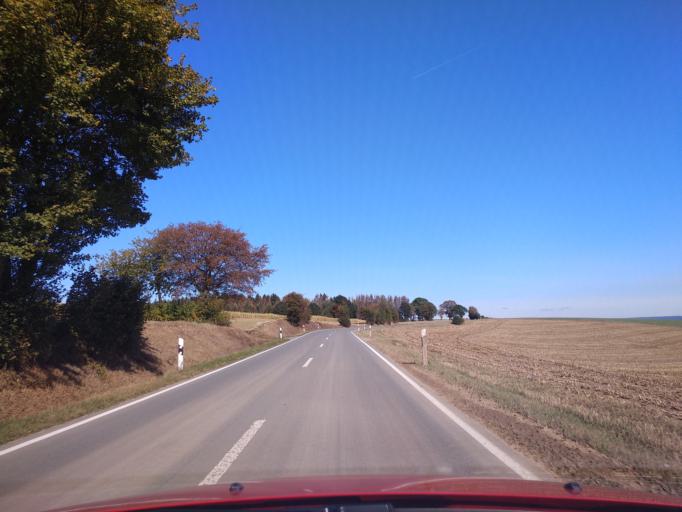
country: DE
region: Lower Saxony
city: Boffzen
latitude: 51.7405
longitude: 9.2994
